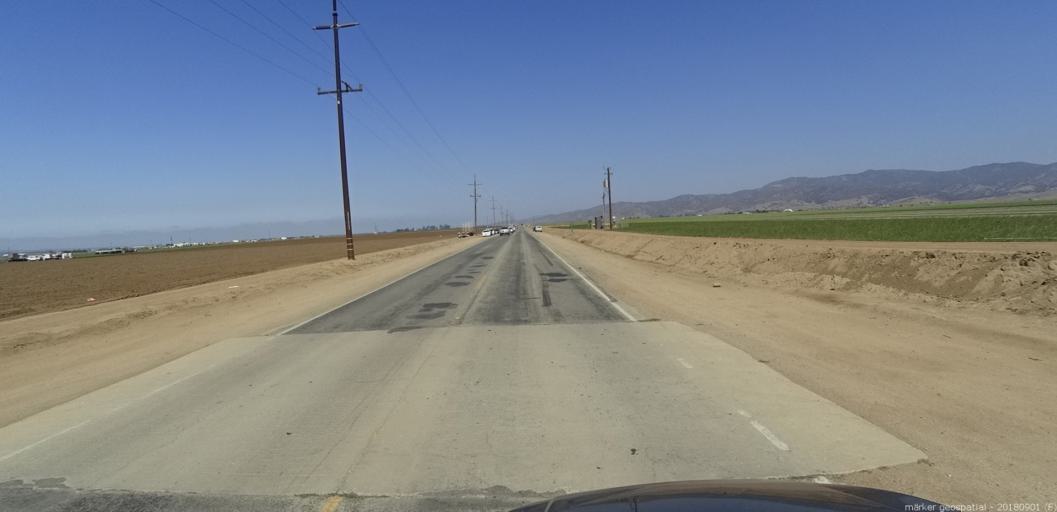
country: US
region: California
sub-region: Monterey County
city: Chualar
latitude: 36.5845
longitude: -121.4995
